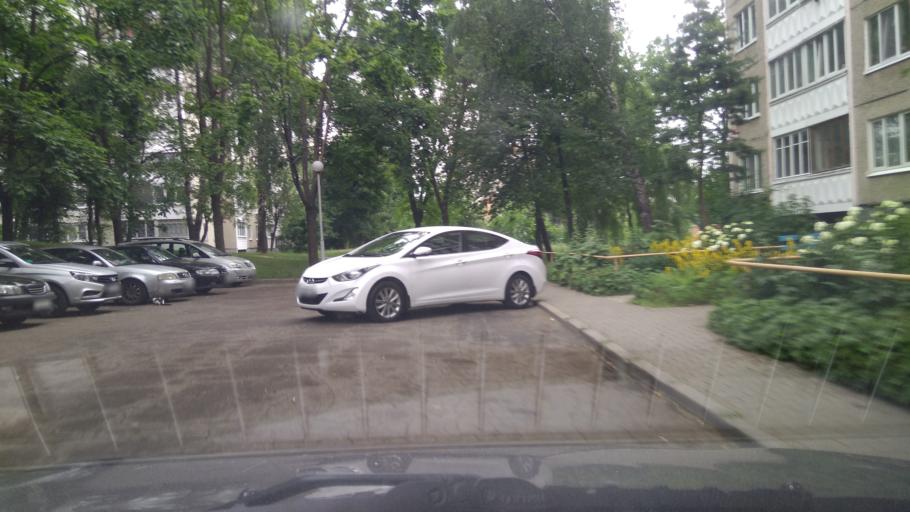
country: BY
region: Minsk
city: Novoye Medvezhino
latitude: 53.8971
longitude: 27.4512
